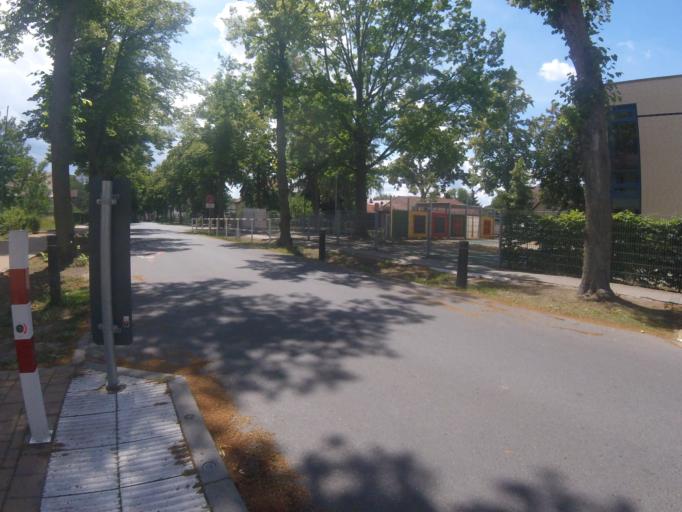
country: DE
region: Brandenburg
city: Bestensee
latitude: 52.2751
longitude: 13.6413
